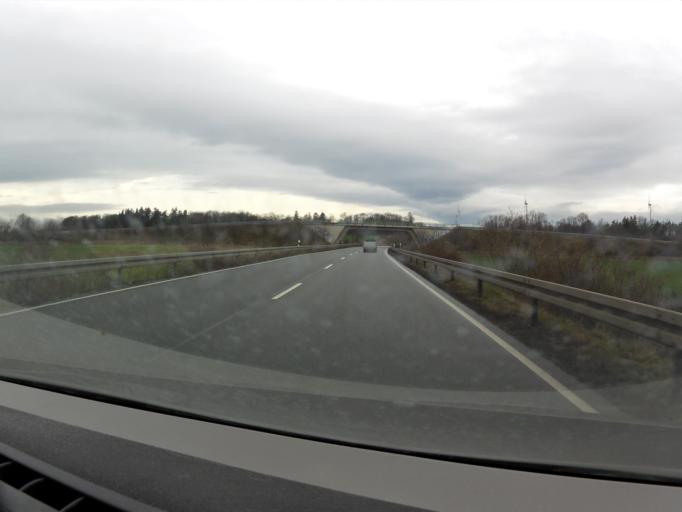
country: DE
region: Saxony-Anhalt
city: Grossorner
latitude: 51.6547
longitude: 11.4615
